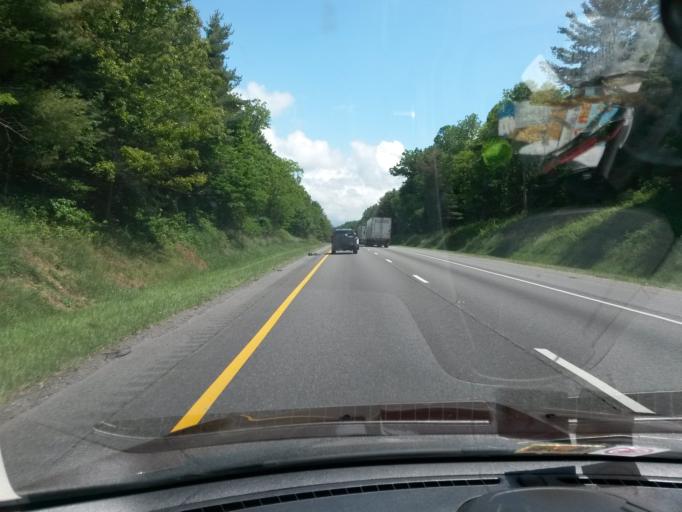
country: US
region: Virginia
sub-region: Carroll County
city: Woodlawn
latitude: 36.7632
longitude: -80.7970
